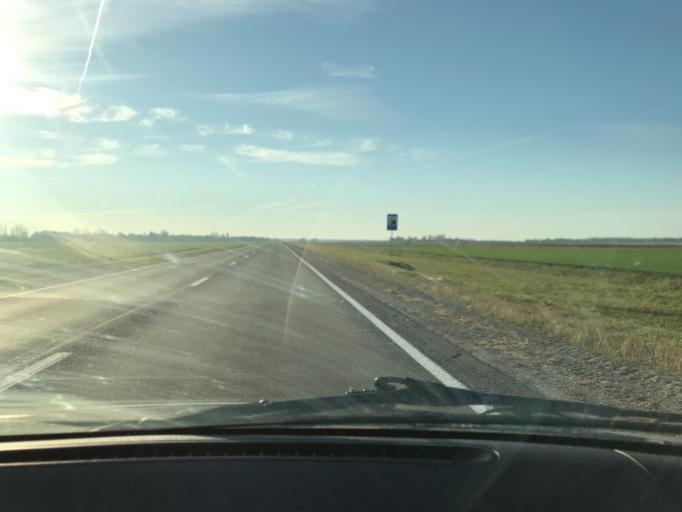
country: BY
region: Brest
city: Antopal'
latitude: 52.2084
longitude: 24.6215
